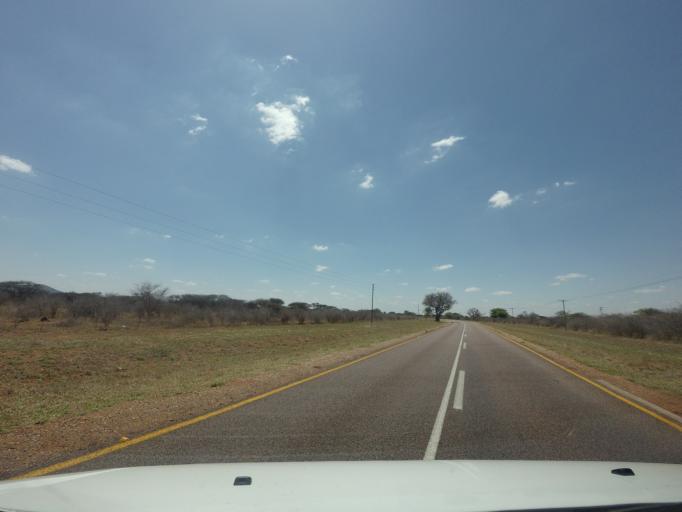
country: ZA
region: Limpopo
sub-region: Waterberg District Municipality
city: Mokopane
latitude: -23.7686
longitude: 28.8911
